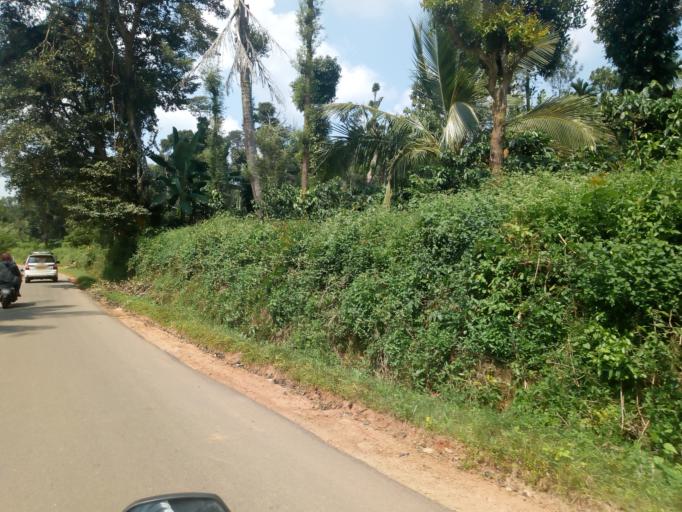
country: IN
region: Karnataka
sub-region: Kodagu
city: Ponnampet
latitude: 12.0301
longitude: 75.9661
